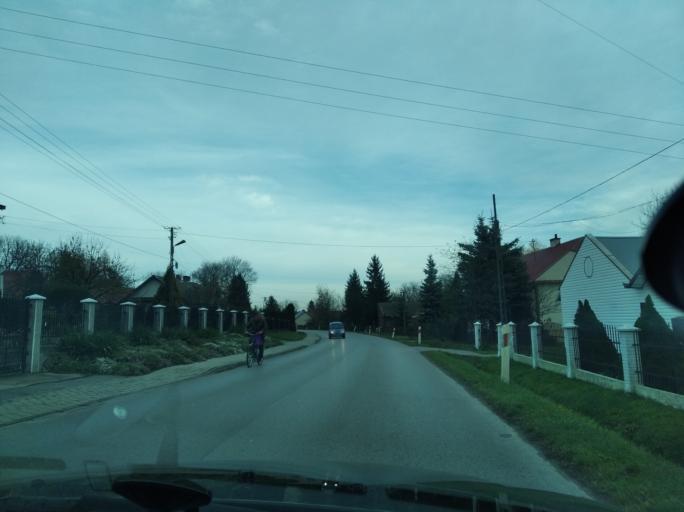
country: PL
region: Subcarpathian Voivodeship
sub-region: Powiat przeworski
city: Przeworsk
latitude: 50.0495
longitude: 22.4667
